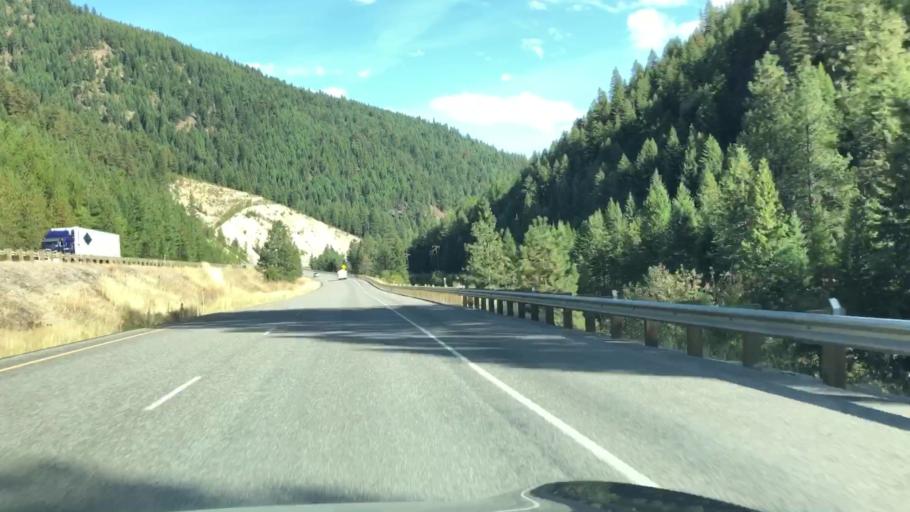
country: US
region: Montana
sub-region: Sanders County
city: Thompson Falls
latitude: 47.3131
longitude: -115.2193
